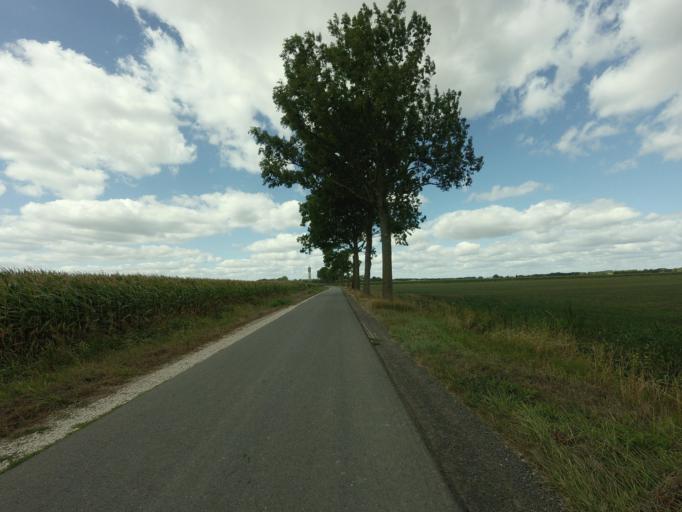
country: NL
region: North Brabant
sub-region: Gemeente Oss
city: Berghem
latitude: 51.8067
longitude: 5.6135
